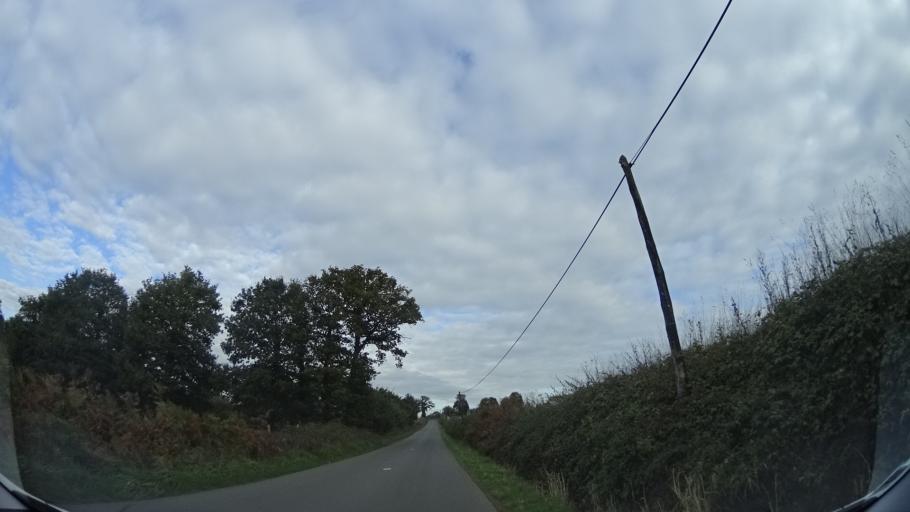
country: FR
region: Brittany
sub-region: Departement d'Ille-et-Vilaine
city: Geveze
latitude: 48.2288
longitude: -1.7864
